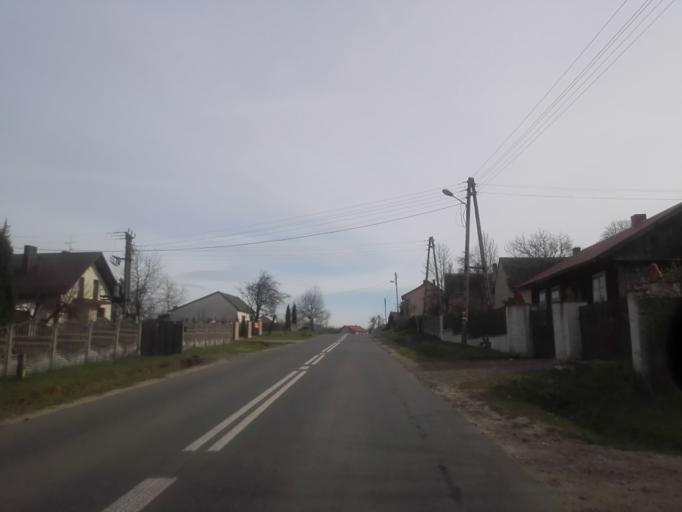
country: PL
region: Silesian Voivodeship
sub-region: Powiat czestochowski
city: Olsztyn
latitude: 50.7298
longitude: 19.3323
